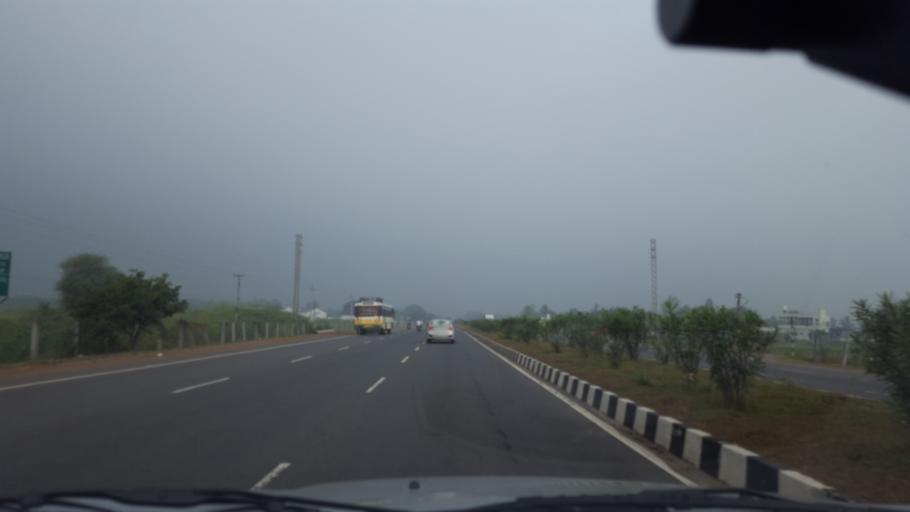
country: IN
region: Andhra Pradesh
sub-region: Prakasam
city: Ongole
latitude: 15.5818
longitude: 80.0400
